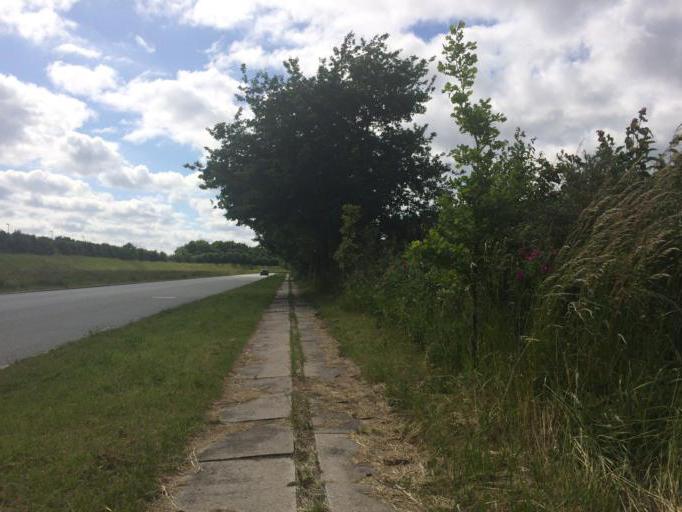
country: DK
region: Capital Region
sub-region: Hvidovre Kommune
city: Hvidovre
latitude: 55.6069
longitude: 12.4566
